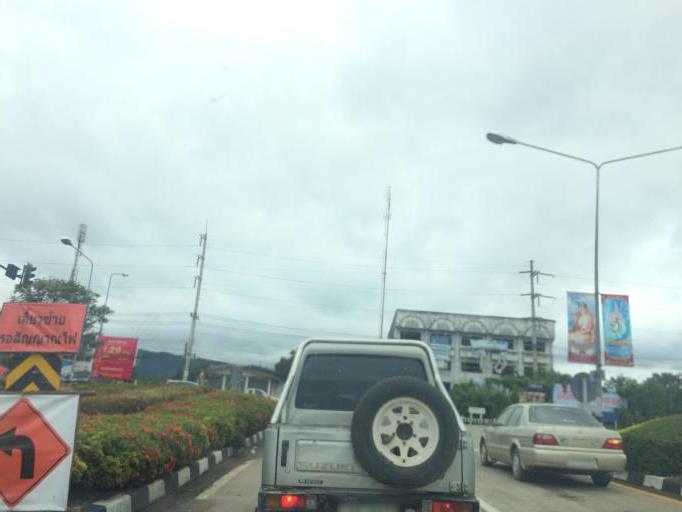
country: TH
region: Chiang Rai
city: Mae Lao
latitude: 19.7462
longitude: 99.7260
